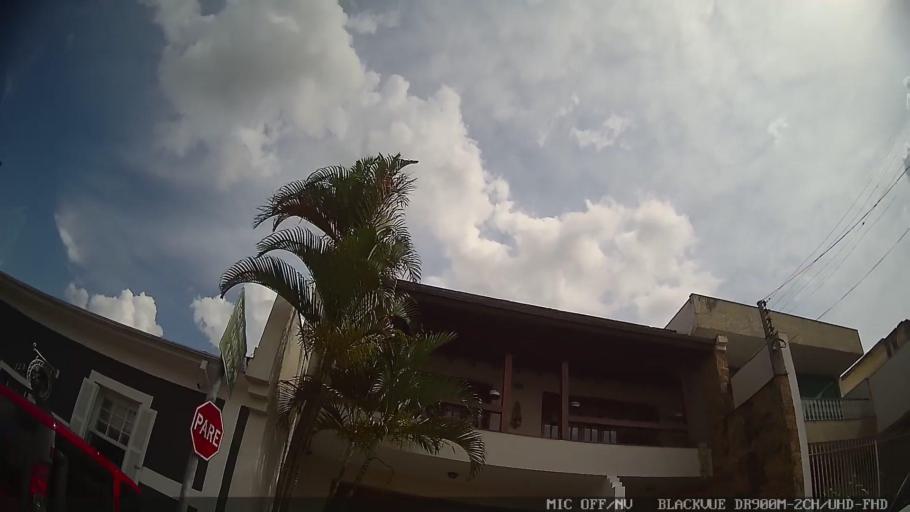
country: BR
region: Sao Paulo
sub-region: Braganca Paulista
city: Braganca Paulista
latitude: -22.9617
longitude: -46.5384
